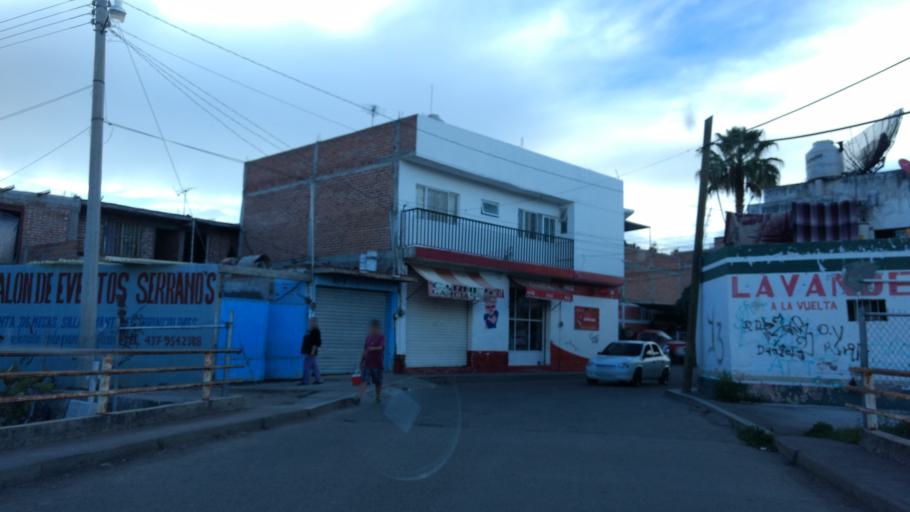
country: MX
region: Zacatecas
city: Tlaltenango de Sanchez Roman
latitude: 21.7805
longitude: -103.2999
